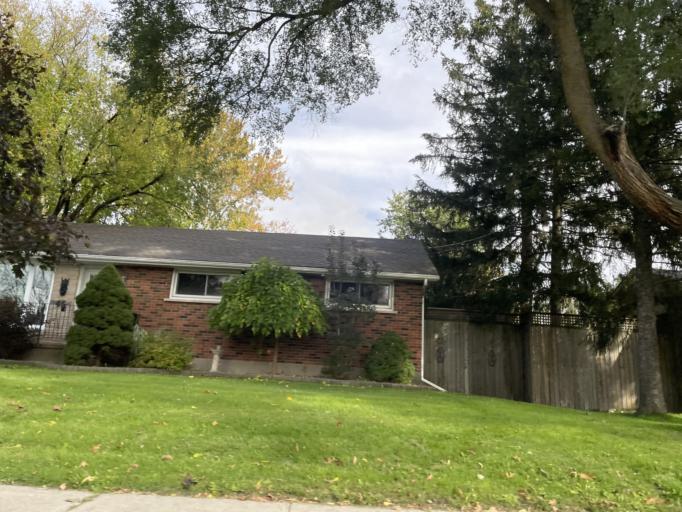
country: CA
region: Ontario
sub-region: Wellington County
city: Guelph
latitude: 43.5350
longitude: -80.2733
